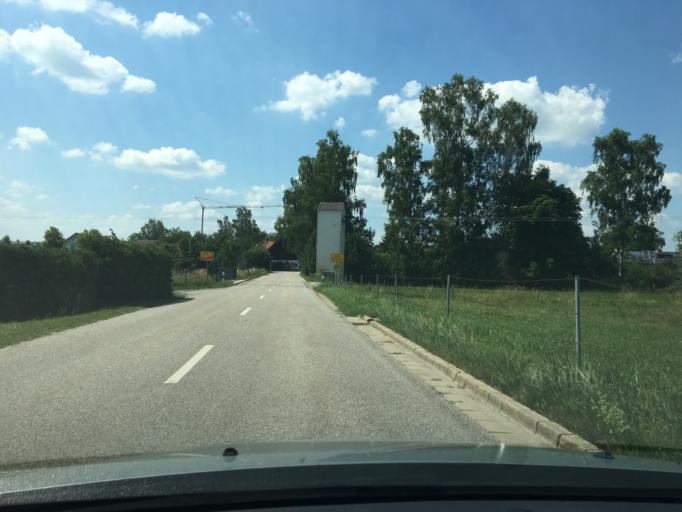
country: DE
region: Bavaria
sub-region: Upper Bavaria
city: Egglkofen
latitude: 48.4268
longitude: 12.4184
